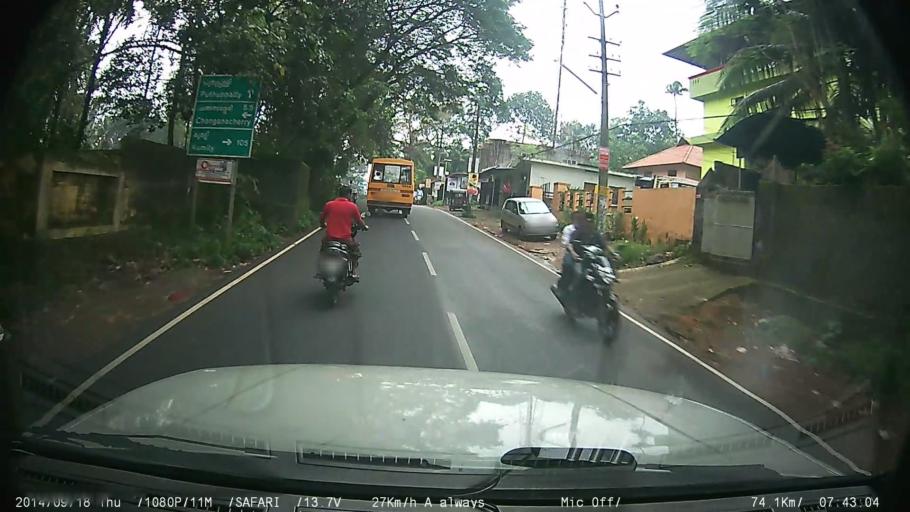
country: IN
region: Kerala
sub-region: Kottayam
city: Changanacheri
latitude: 9.4723
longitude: 76.5770
